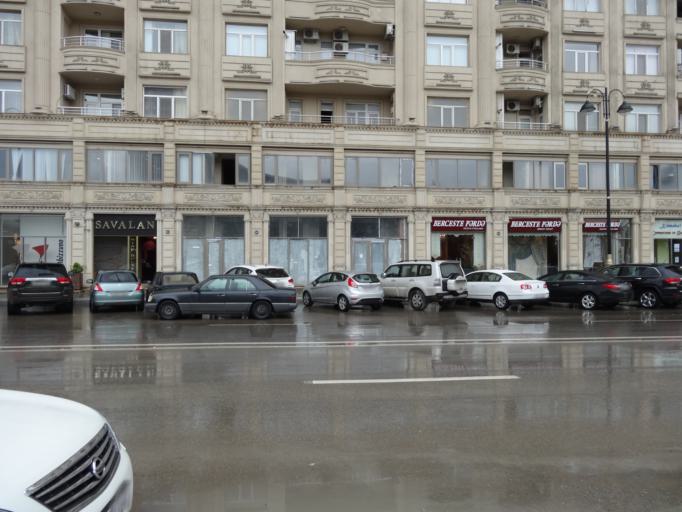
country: AZ
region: Baki
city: Baku
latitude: 40.3974
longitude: 49.8691
